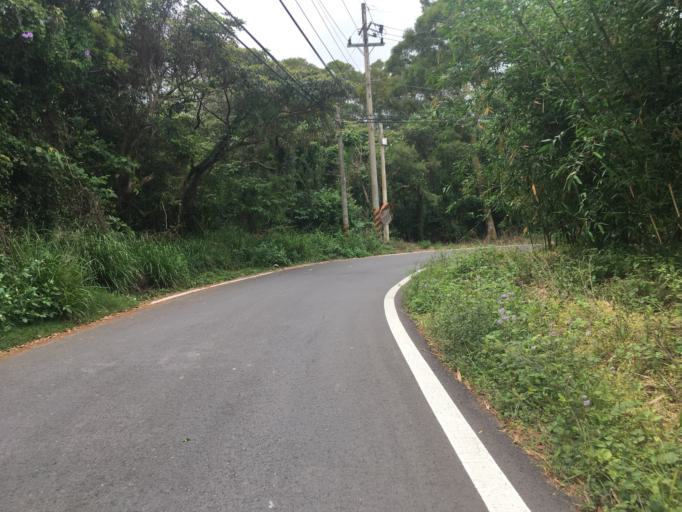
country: TW
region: Taiwan
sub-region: Hsinchu
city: Hsinchu
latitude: 24.7480
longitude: 120.9843
